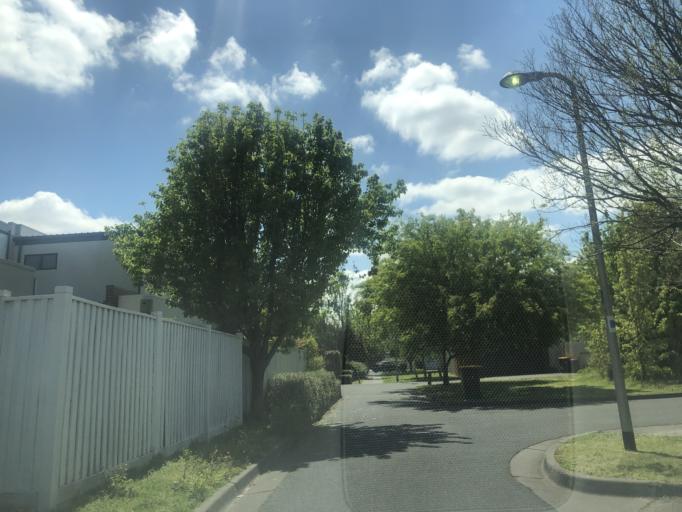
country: AU
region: Victoria
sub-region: Monash
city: Mulgrave
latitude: -37.9241
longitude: 145.1860
